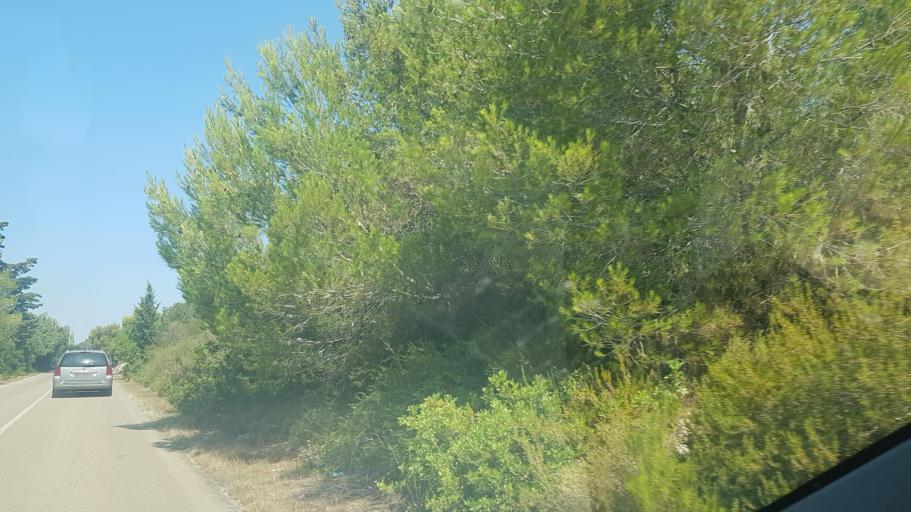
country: IT
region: Apulia
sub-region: Provincia di Lecce
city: Otranto
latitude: 40.1929
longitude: 18.4406
